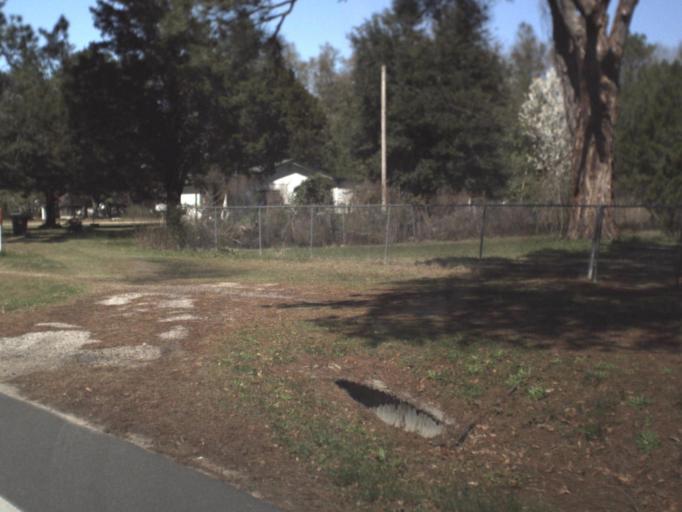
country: US
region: Florida
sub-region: Gadsden County
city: Gretna
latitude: 30.6240
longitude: -84.6674
